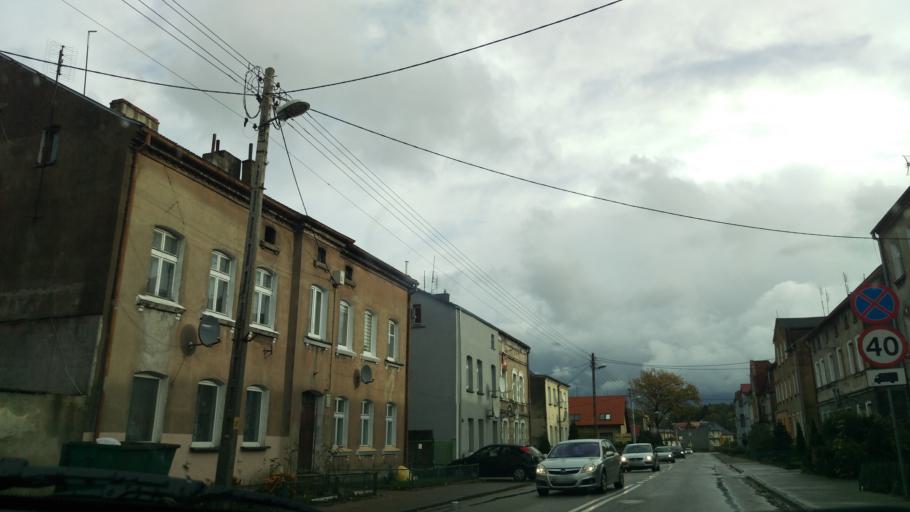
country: PL
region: West Pomeranian Voivodeship
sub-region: Powiat gryficki
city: Ploty
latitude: 53.8059
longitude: 15.2667
